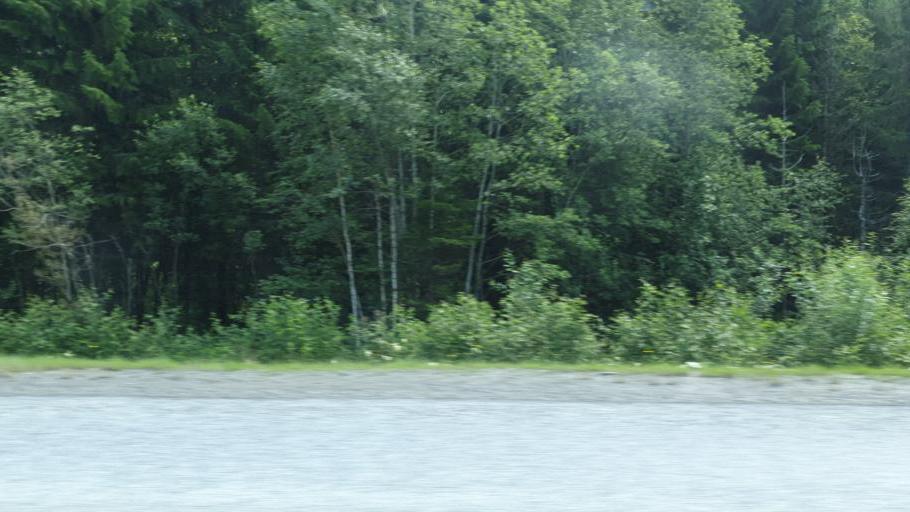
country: NO
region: Sor-Trondelag
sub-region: Midtre Gauldal
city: Storen
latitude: 63.0038
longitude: 10.2383
